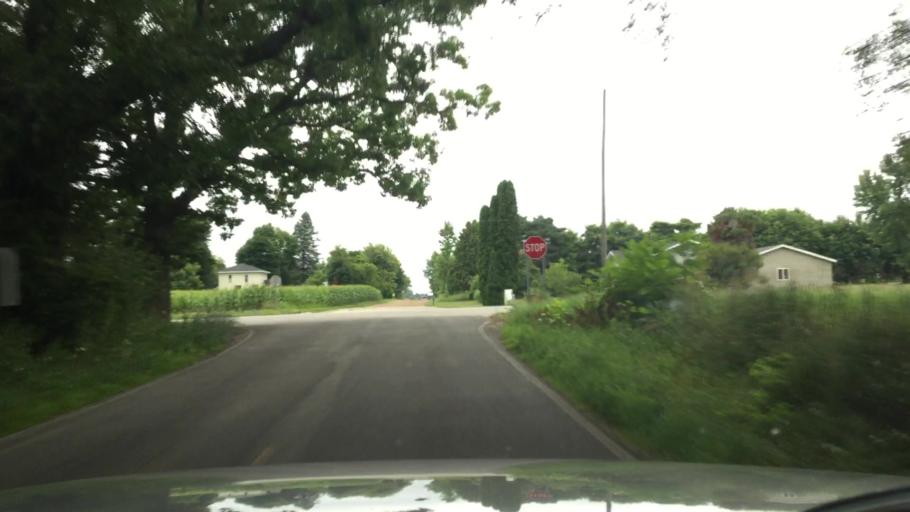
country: US
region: Michigan
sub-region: Montcalm County
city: Greenville
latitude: 43.1920
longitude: -85.2231
